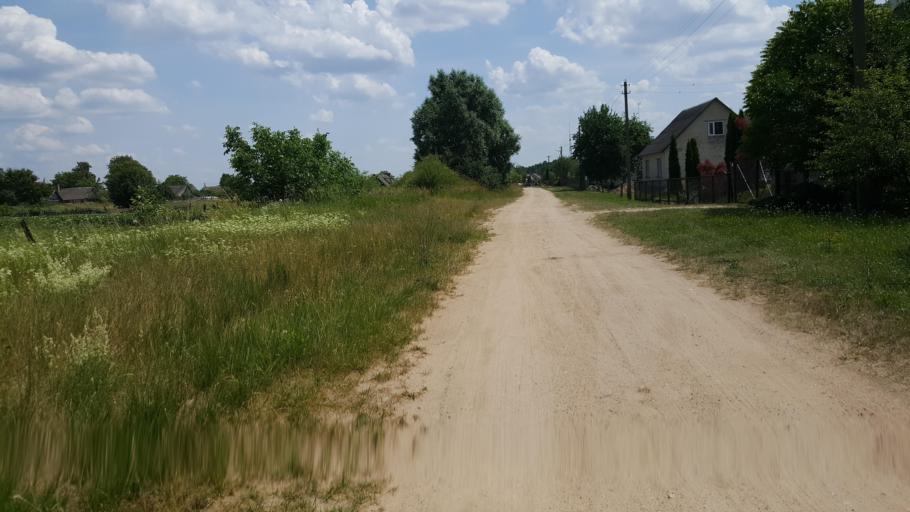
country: BY
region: Brest
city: Kamyanyets
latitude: 52.4036
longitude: 23.7878
